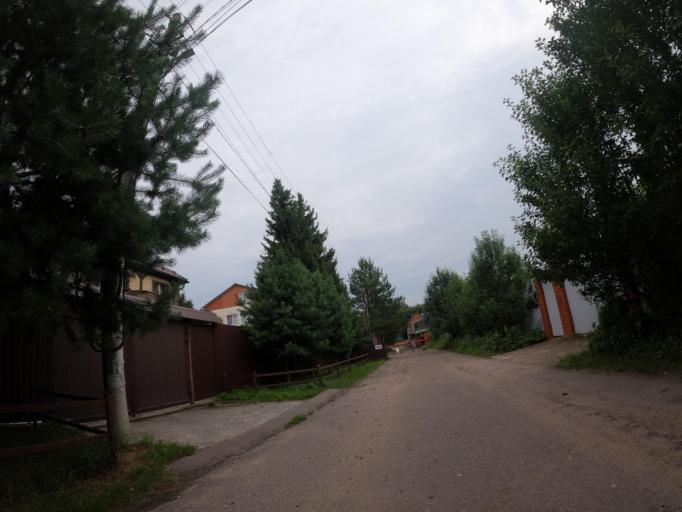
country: RU
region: Moskovskaya
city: Bykovo
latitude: 55.6533
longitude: 38.1093
